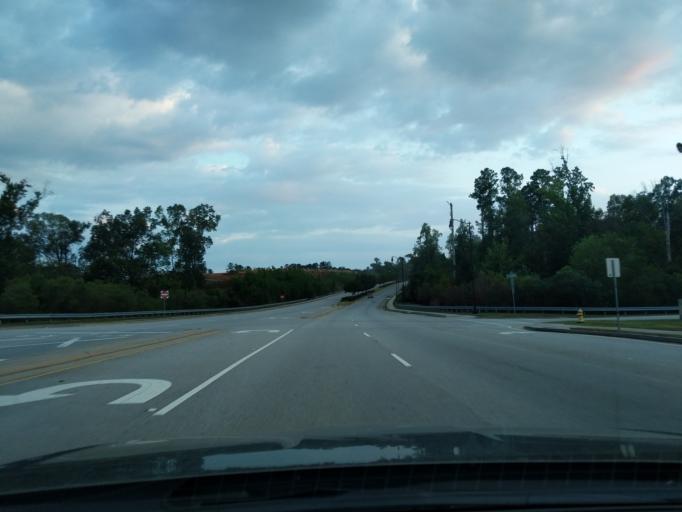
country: US
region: Georgia
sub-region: Columbia County
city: Martinez
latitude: 33.5207
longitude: -82.0240
